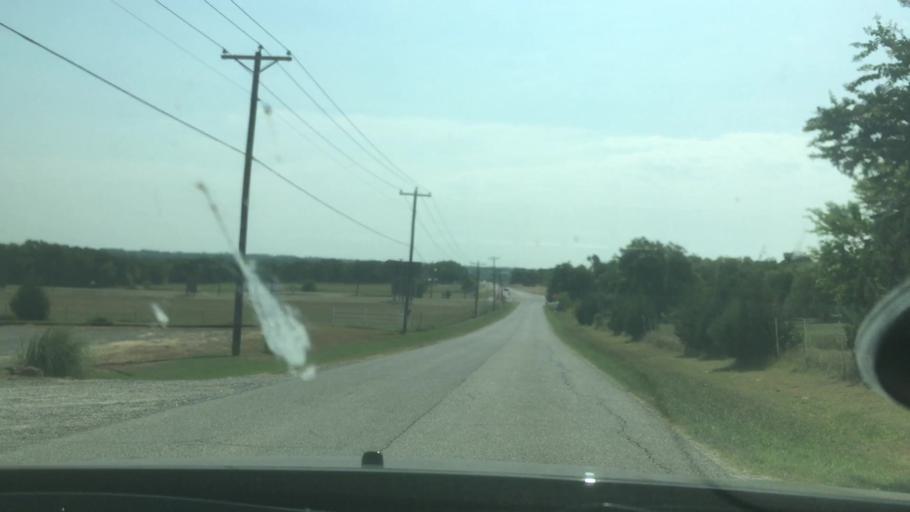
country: US
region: Texas
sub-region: Grayson County
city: Pottsboro
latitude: 33.8021
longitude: -96.6811
